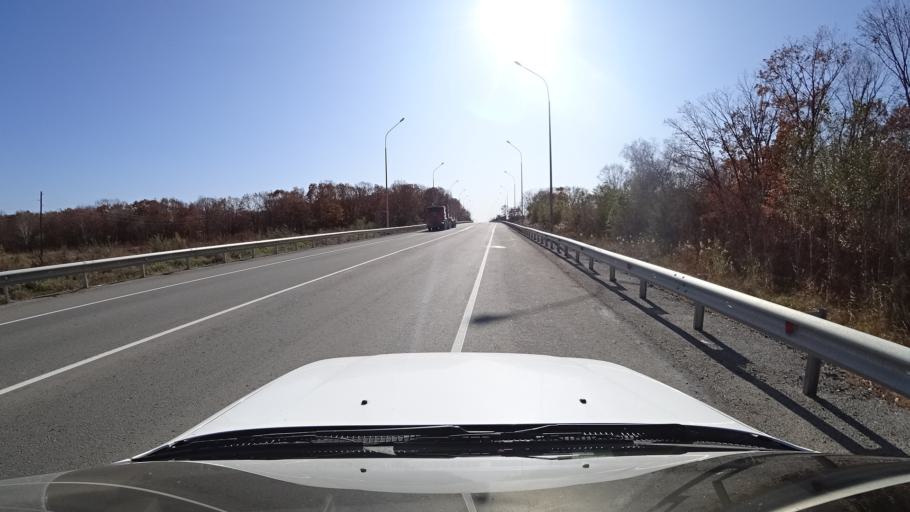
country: RU
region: Primorskiy
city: Dal'nerechensk
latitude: 45.8849
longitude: 133.7304
